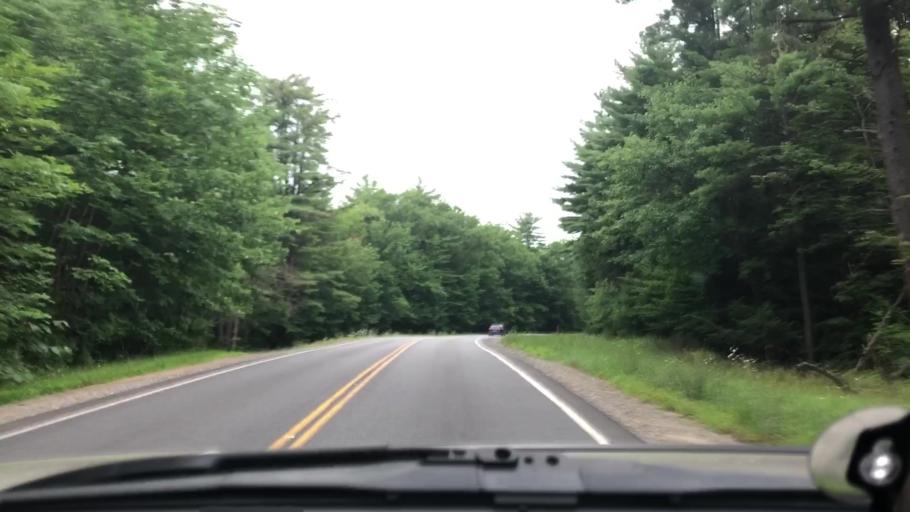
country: US
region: New York
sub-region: Saratoga County
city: Corinth
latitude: 43.2002
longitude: -73.7639
